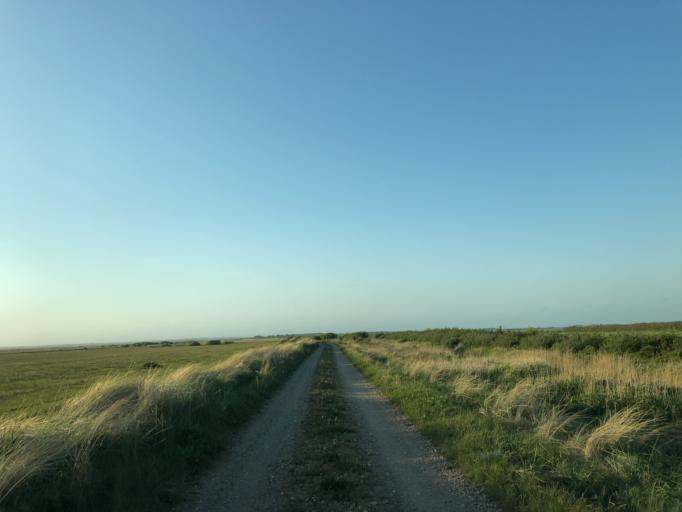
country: DK
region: Central Jutland
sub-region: Ringkobing-Skjern Kommune
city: Ringkobing
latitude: 56.2105
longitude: 8.1628
